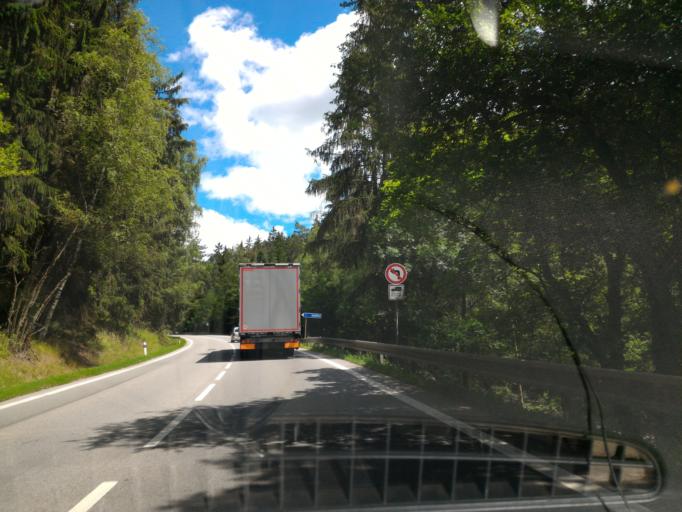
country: CZ
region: Vysocina
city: Velky Beranov
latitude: 49.4063
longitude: 15.6364
